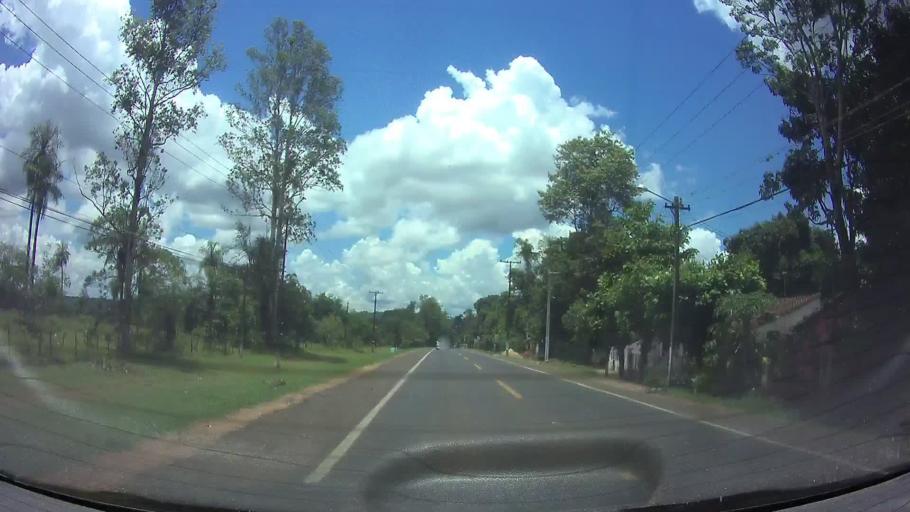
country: PY
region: Central
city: Capiata
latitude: -25.3541
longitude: -57.4213
